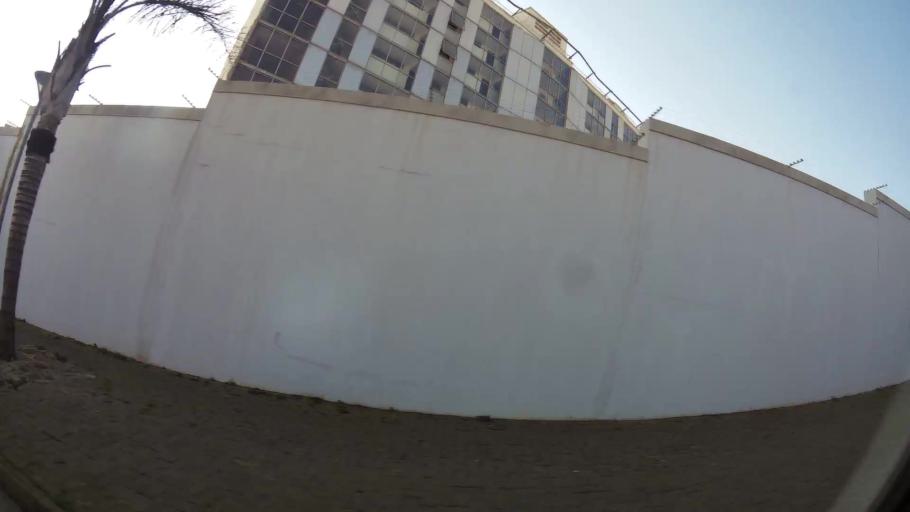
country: ZA
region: Gauteng
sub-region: Ekurhuleni Metropolitan Municipality
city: Germiston
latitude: -26.1930
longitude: 28.1189
